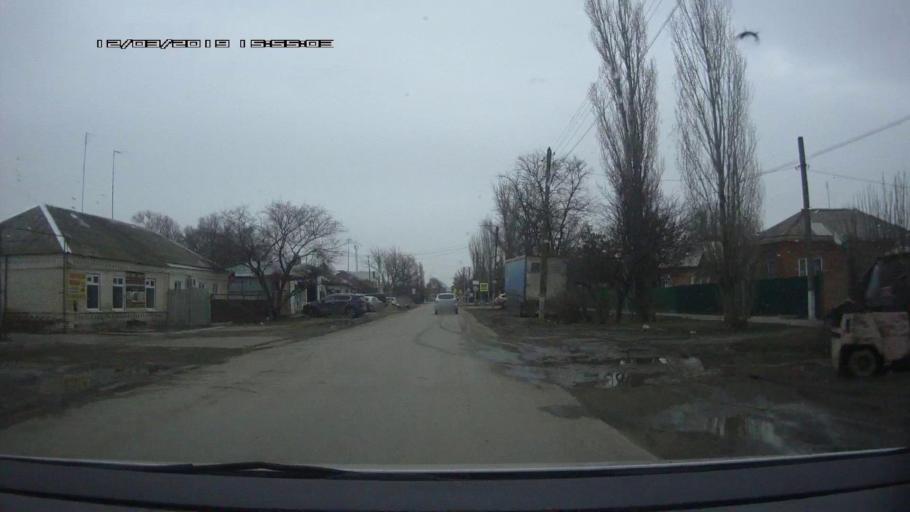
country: RU
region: Rostov
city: Novobataysk
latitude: 46.8944
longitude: 39.7790
